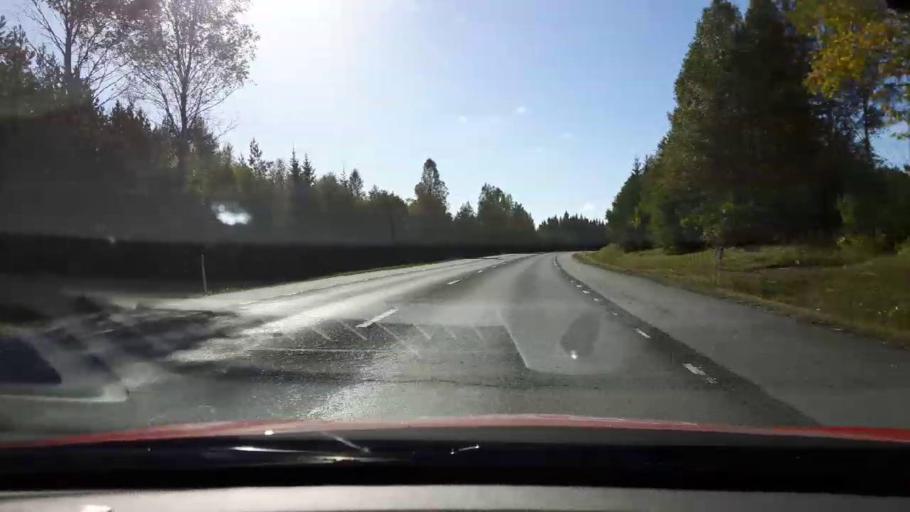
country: SE
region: Vaesternorrland
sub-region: Ange Kommun
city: Ange
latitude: 62.6732
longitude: 15.6017
